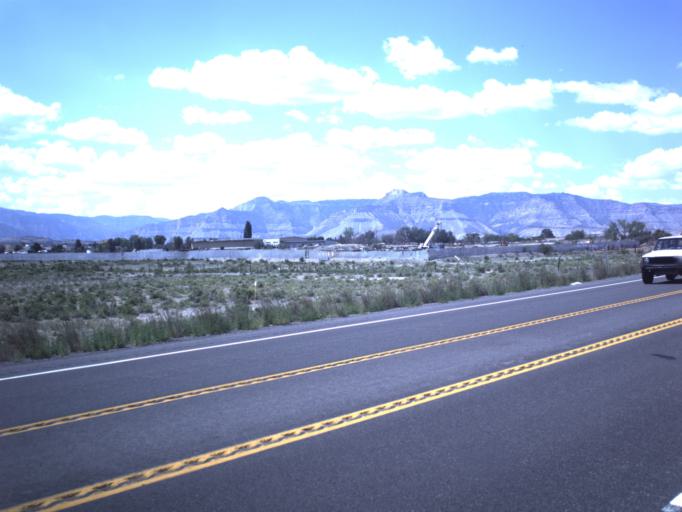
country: US
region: Utah
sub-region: Emery County
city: Huntington
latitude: 39.3145
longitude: -110.9643
